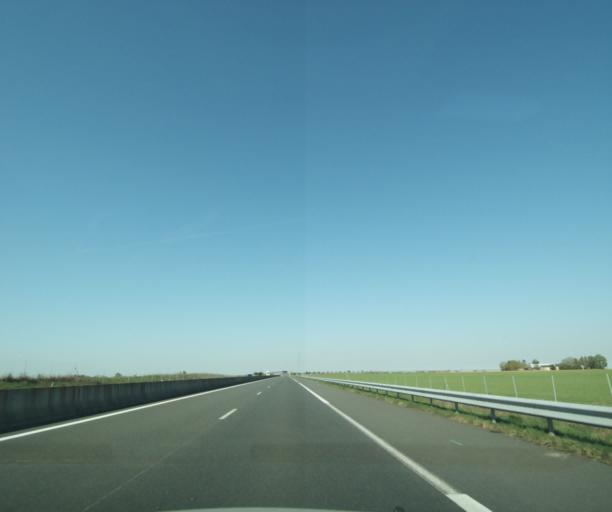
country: FR
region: Centre
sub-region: Departement du Loiret
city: Chevilly
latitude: 48.0471
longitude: 1.8981
